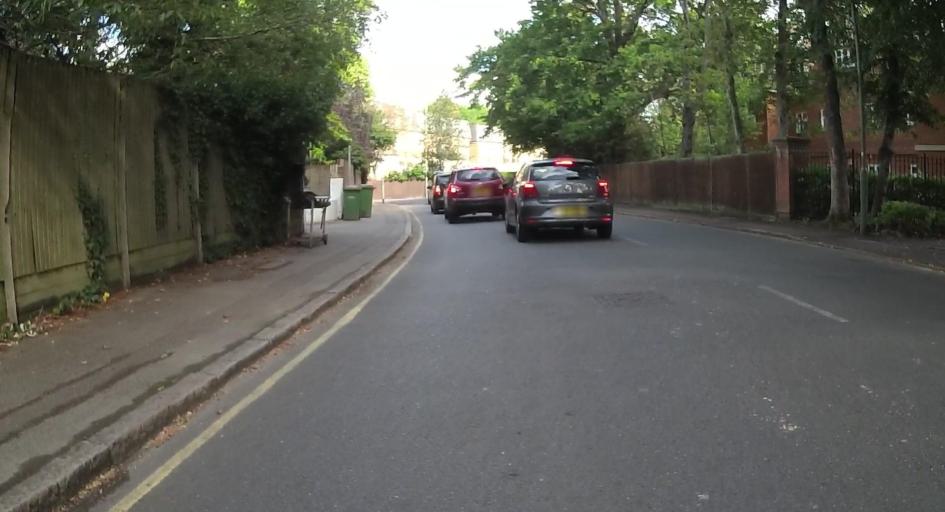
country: GB
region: England
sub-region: Surrey
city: Weybridge
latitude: 51.3658
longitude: -0.4426
